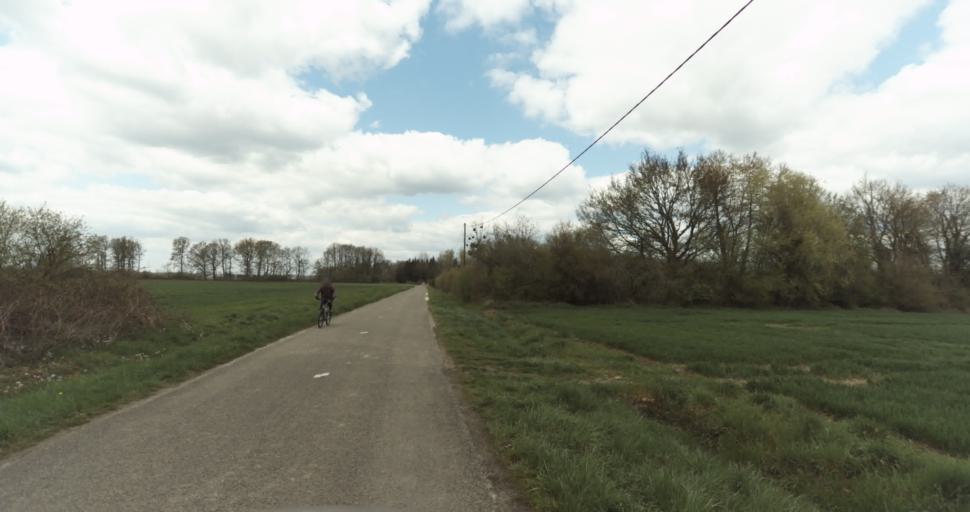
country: FR
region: Bourgogne
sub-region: Departement de la Cote-d'Or
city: Auxonne
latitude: 47.1787
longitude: 5.4203
